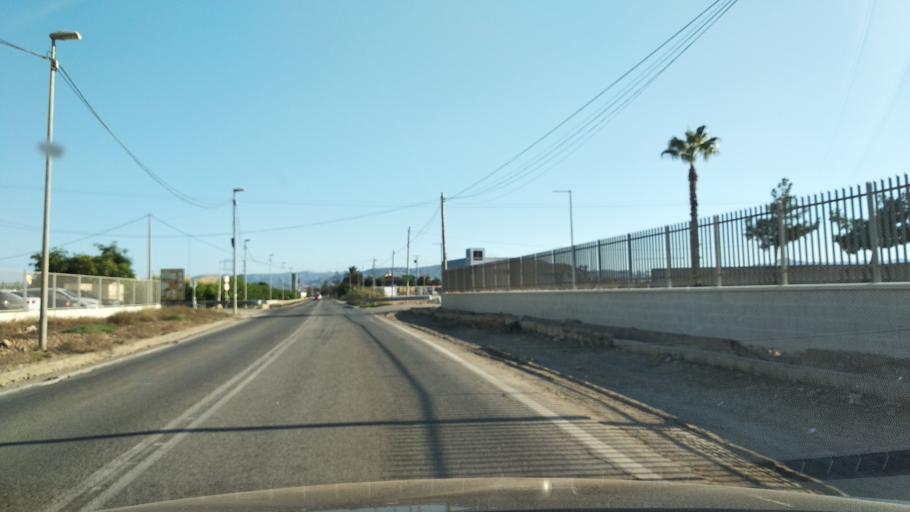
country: ES
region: Murcia
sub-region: Murcia
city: Santomera
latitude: 38.0497
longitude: -1.0556
